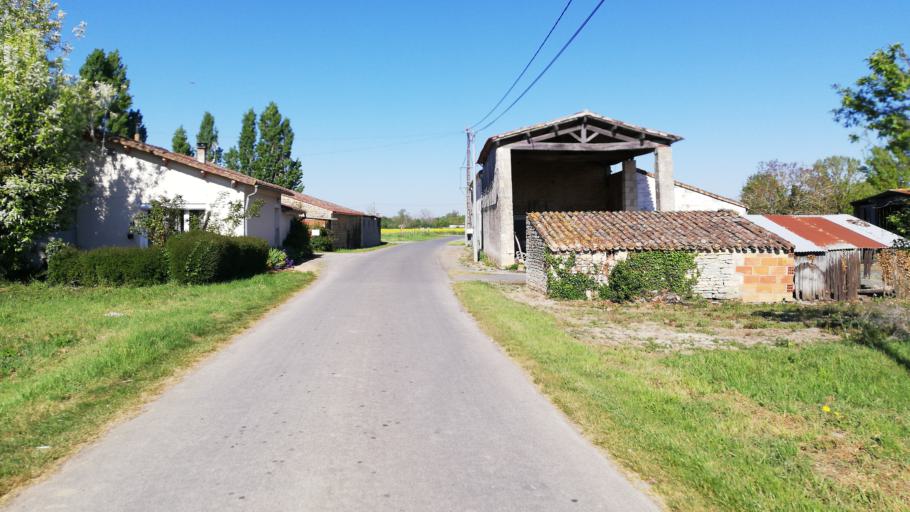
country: FR
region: Pays de la Loire
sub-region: Departement de la Vendee
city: Maillezais
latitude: 46.3262
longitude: -0.7450
